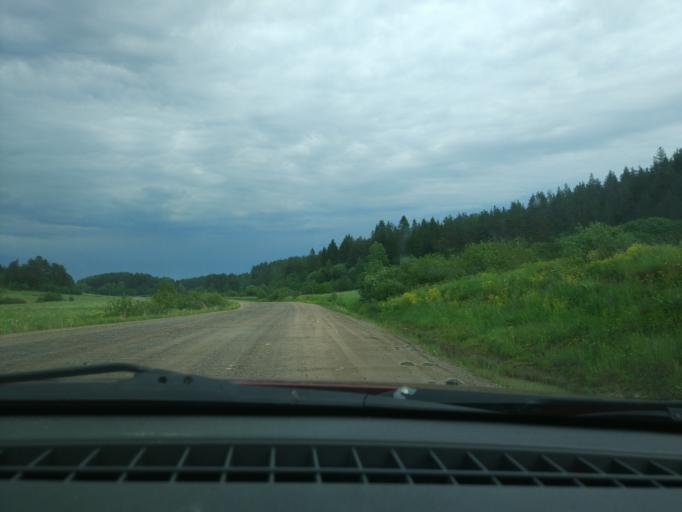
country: RU
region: Leningrad
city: Kuznechnoye
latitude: 61.2754
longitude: 29.8453
